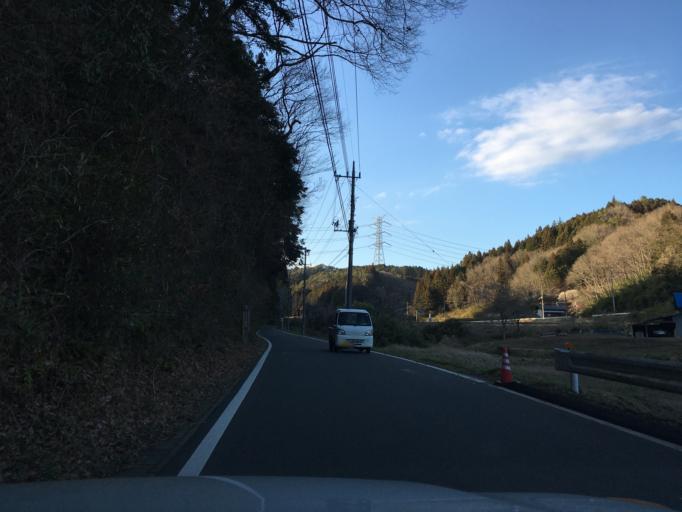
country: JP
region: Tochigi
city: Otawara
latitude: 36.8413
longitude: 140.1885
